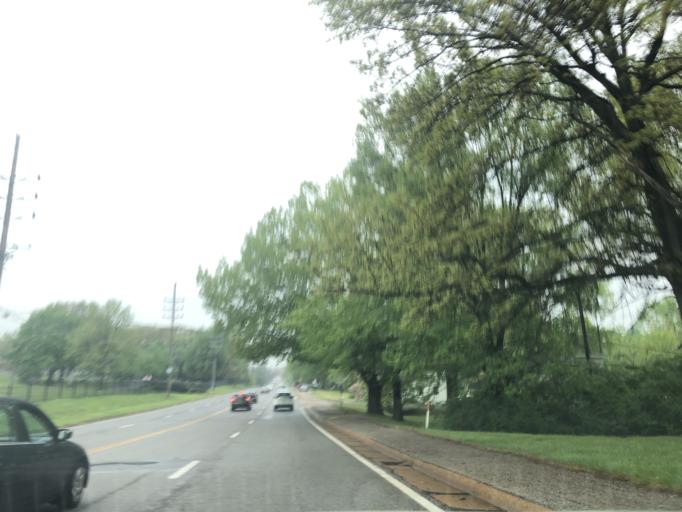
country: US
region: Missouri
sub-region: Saint Louis County
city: Marlborough
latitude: 38.5761
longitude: -90.3190
